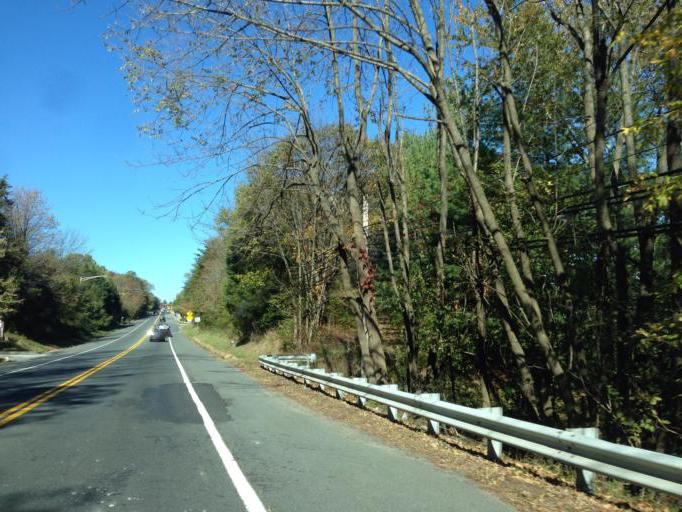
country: US
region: Maryland
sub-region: Montgomery County
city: Damascus
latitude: 39.2687
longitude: -77.2174
